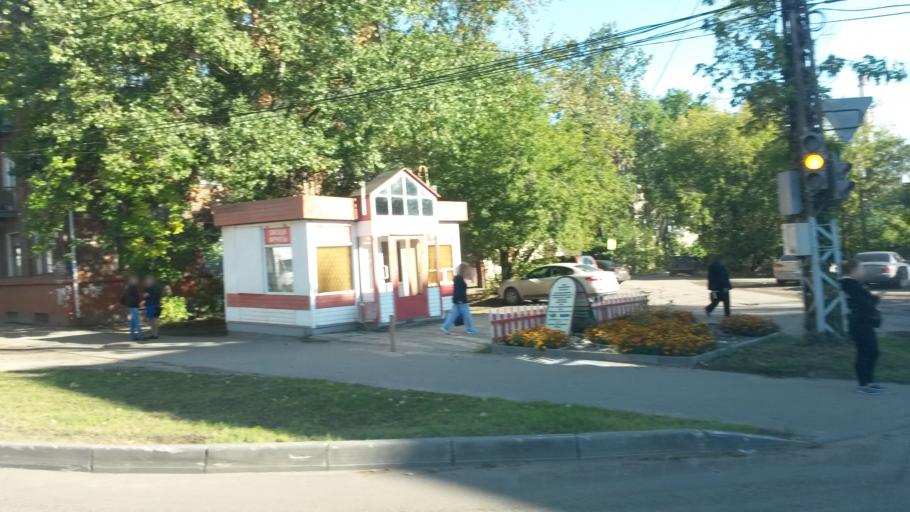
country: RU
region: Ivanovo
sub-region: Gorod Ivanovo
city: Ivanovo
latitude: 57.0014
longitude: 40.9609
